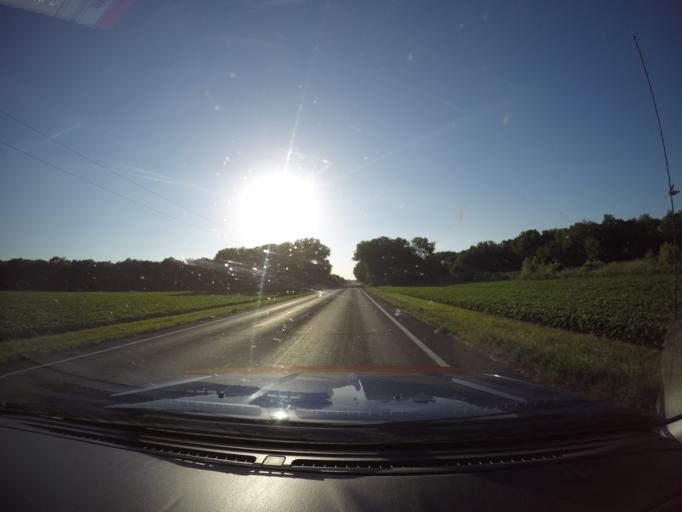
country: US
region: Kansas
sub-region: Pottawatomie County
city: Saint Marys
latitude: 39.2042
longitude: -96.0953
